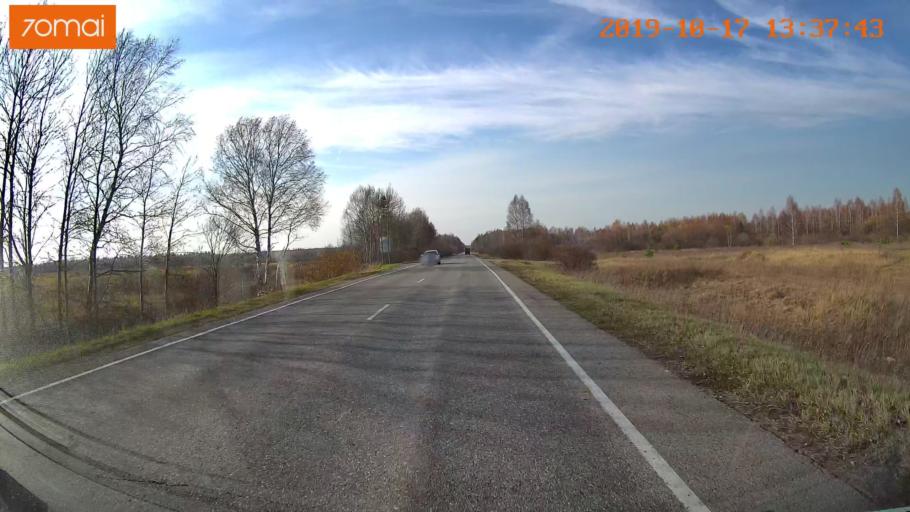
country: RU
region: Rjazan
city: Tuma
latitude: 55.1423
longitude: 40.6319
